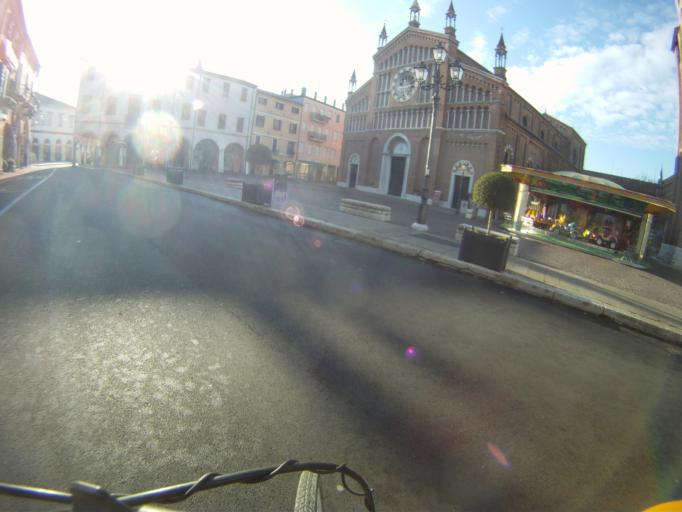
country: IT
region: Veneto
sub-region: Provincia di Padova
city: Piove di Sacco-Piovega
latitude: 45.2966
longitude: 12.0350
